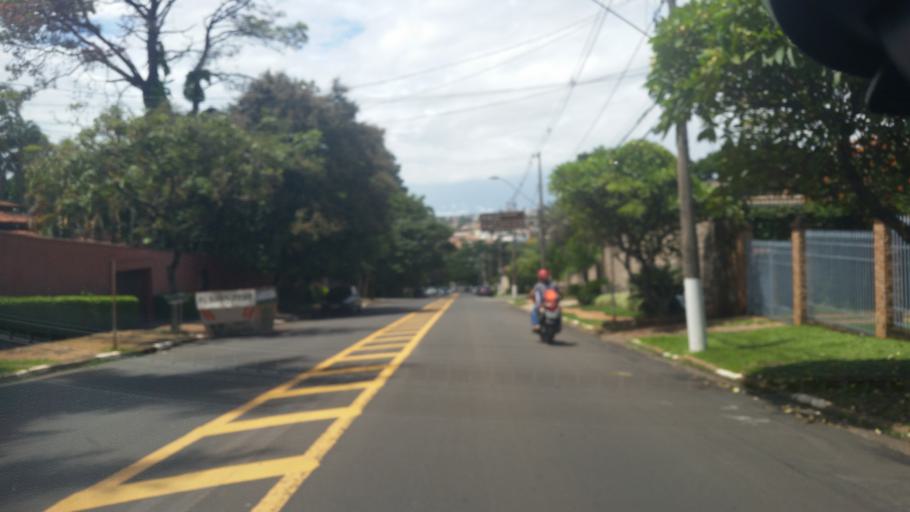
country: BR
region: Sao Paulo
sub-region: Campinas
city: Campinas
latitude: -22.8694
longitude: -47.0512
